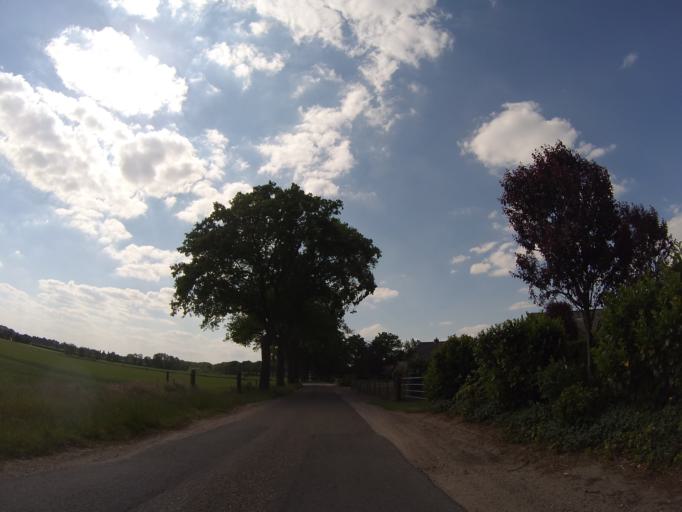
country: NL
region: Gelderland
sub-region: Gemeente Barneveld
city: Zwartebroek
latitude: 52.1499
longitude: 5.4733
